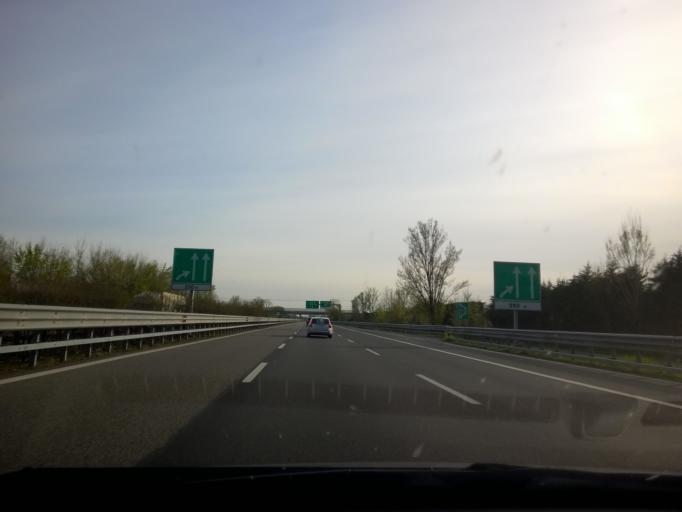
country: IT
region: Lombardy
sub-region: Provincia di Brescia
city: Leno
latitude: 45.3754
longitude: 10.1747
